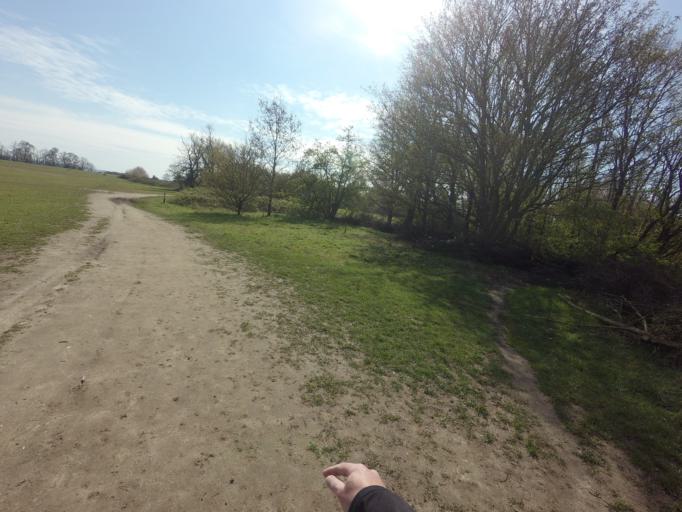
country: NL
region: Limburg
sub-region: Gemeente Maastricht
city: Maastricht
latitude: 50.8327
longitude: 5.6820
